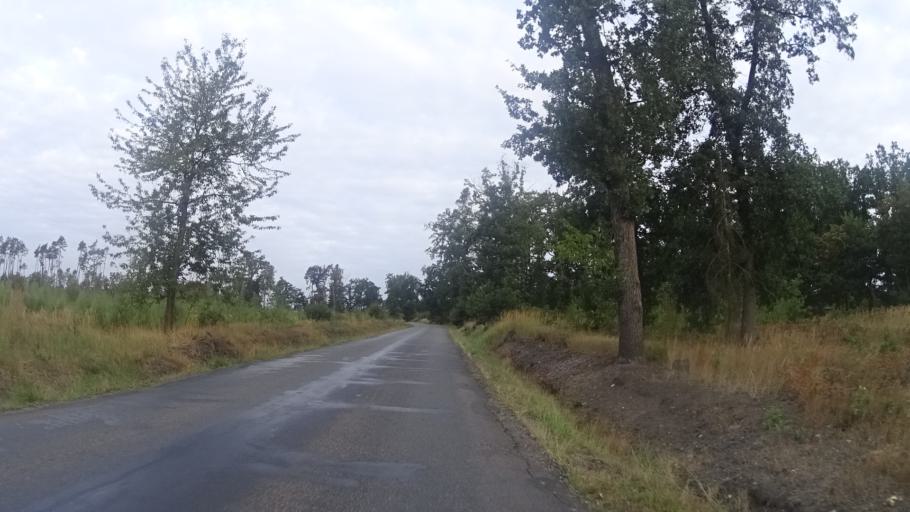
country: CZ
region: Kralovehradecky
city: Cernilov
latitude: 50.2076
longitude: 15.9223
